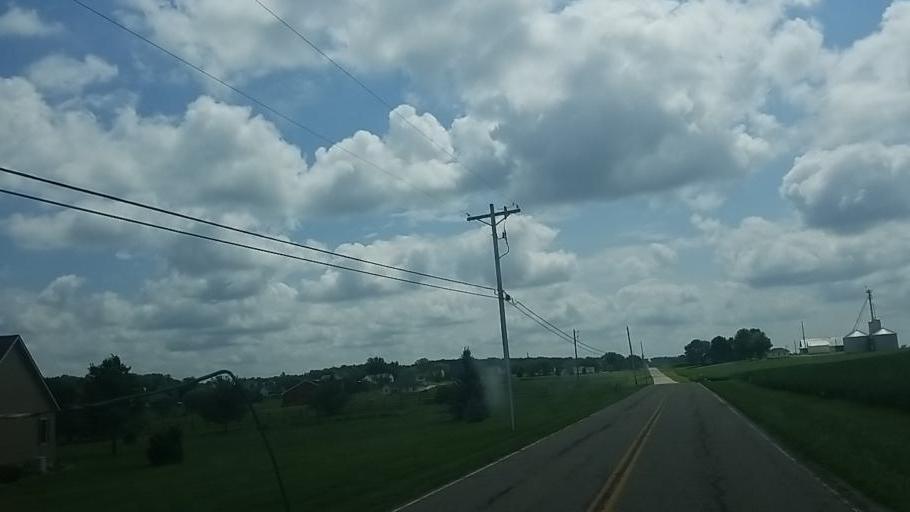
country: US
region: Ohio
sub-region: Fairfield County
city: Lithopolis
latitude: 39.7609
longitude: -82.7632
